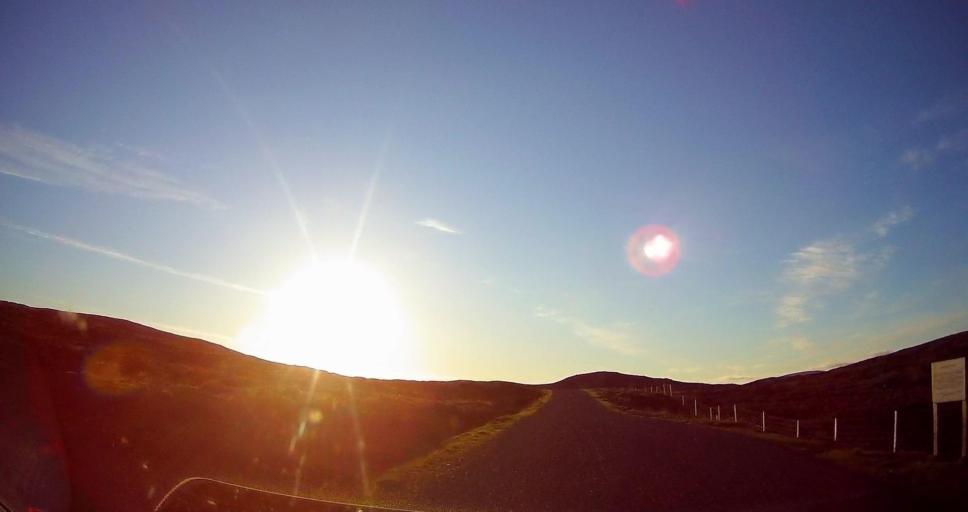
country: GB
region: Scotland
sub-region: Shetland Islands
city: Lerwick
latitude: 60.4415
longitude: -1.4024
